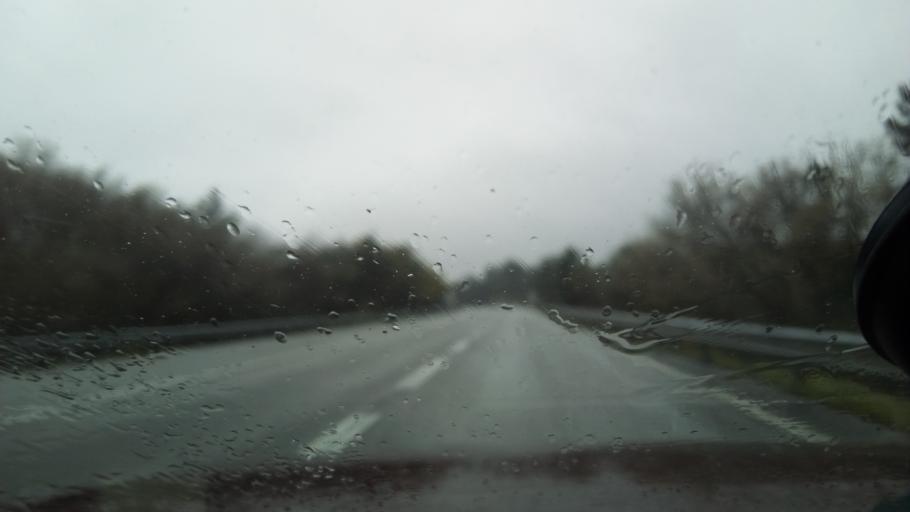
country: PT
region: Guarda
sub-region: Fornos de Algodres
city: Fornos de Algodres
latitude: 40.6106
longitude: -7.5923
